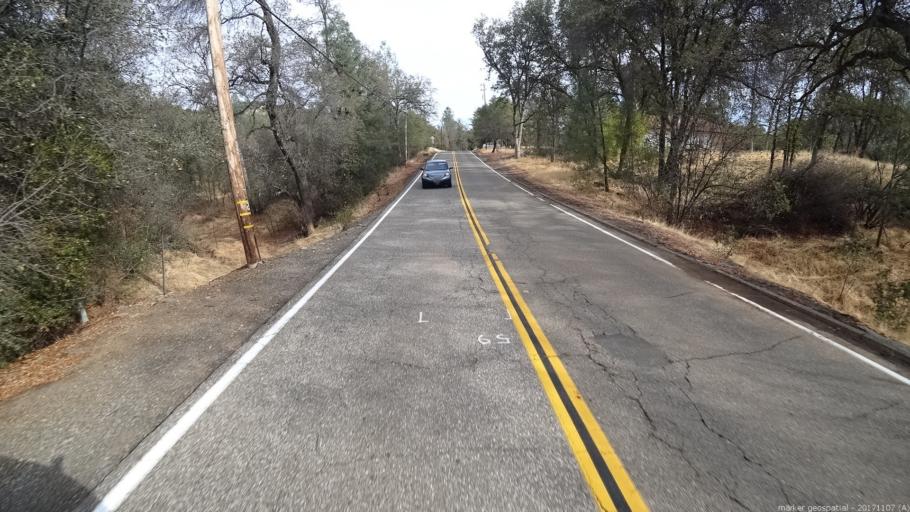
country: US
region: California
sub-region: Shasta County
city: Shasta
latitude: 40.5165
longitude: -122.5065
